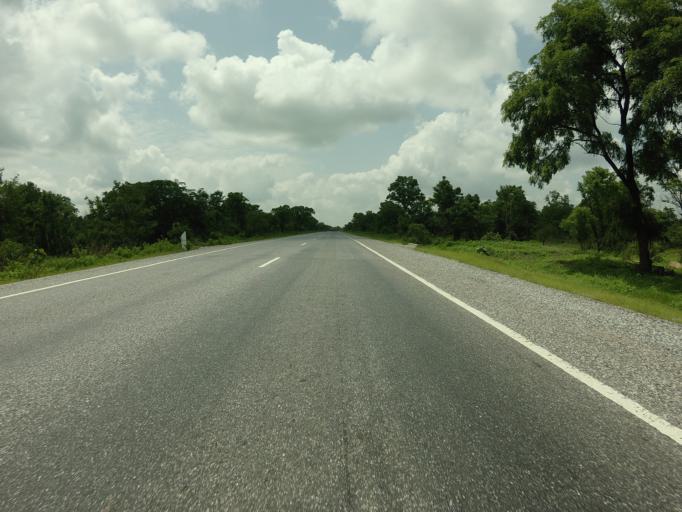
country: GH
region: Northern
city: Tamale
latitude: 9.1500
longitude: -1.3857
